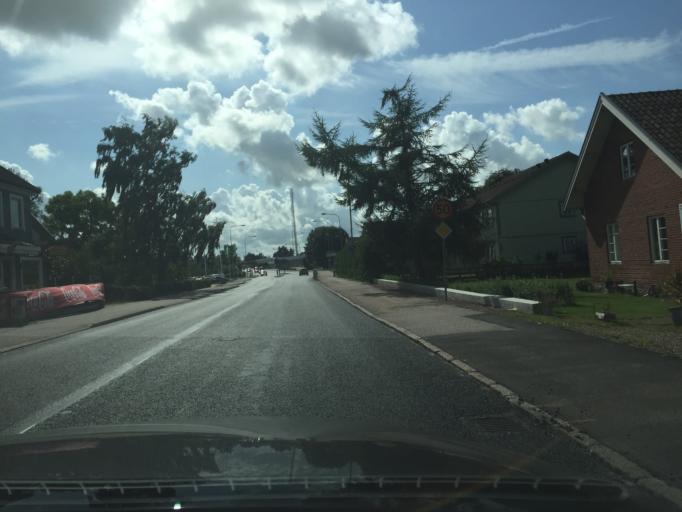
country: SE
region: Halland
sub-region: Laholms Kommun
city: Laholm
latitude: 56.5062
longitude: 13.0355
